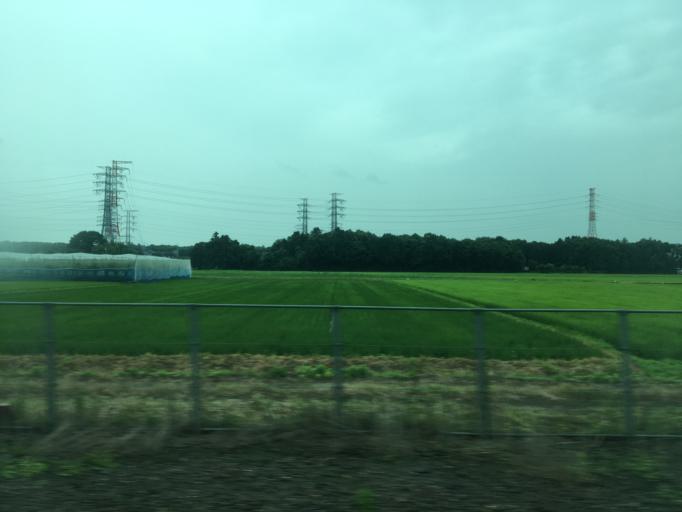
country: JP
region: Ibaraki
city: Koga
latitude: 36.2462
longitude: 139.7509
